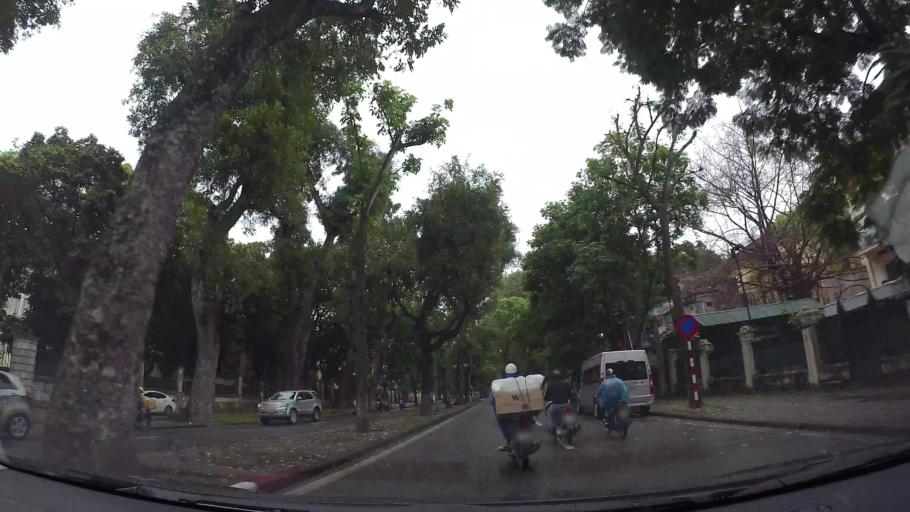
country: VN
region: Ha Noi
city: Hoan Kiem
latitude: 21.0412
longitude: 105.8401
